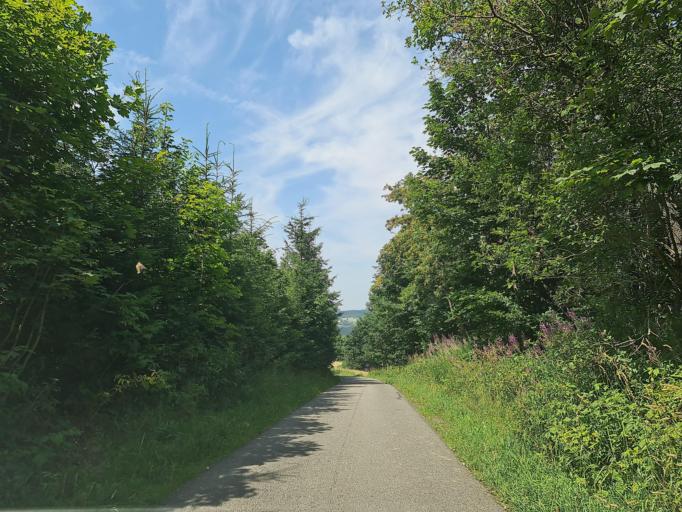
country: DE
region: Saxony
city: Neuhausen
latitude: 50.6595
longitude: 13.4726
